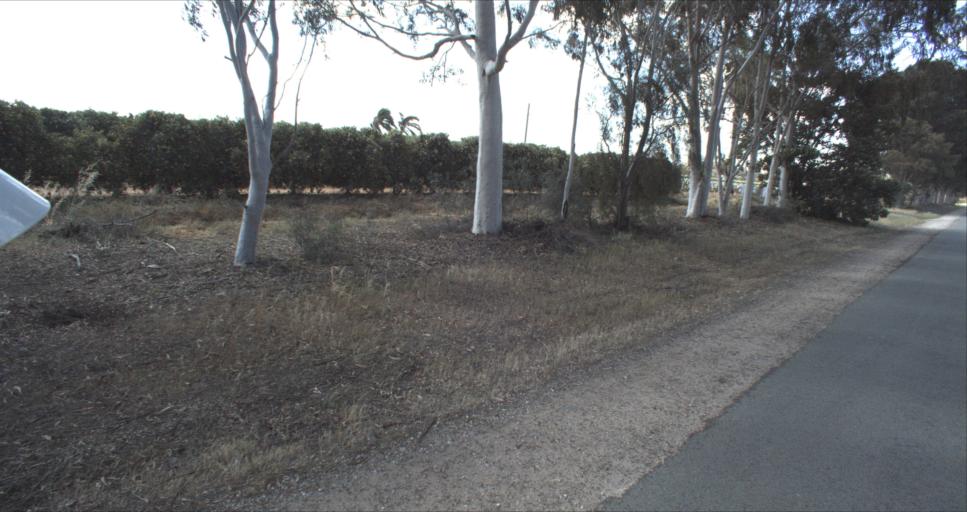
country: AU
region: New South Wales
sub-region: Leeton
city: Leeton
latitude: -34.5101
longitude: 146.2286
